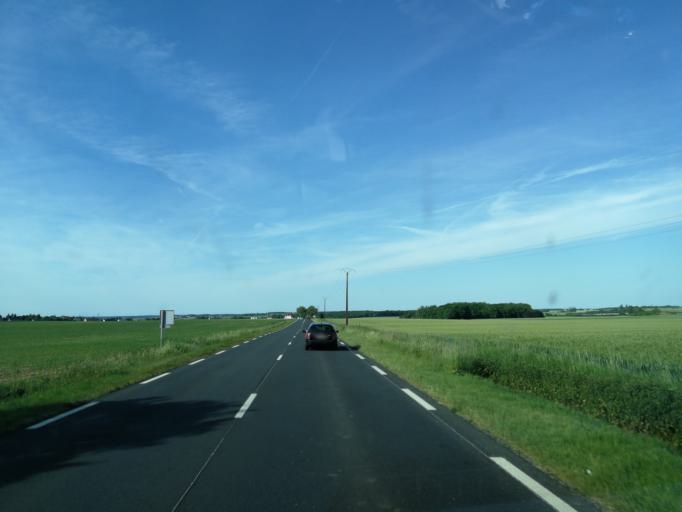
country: FR
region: Centre
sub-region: Departement du Loir-et-Cher
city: Saint-Amand-Longpre
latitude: 47.7090
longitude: 1.0102
